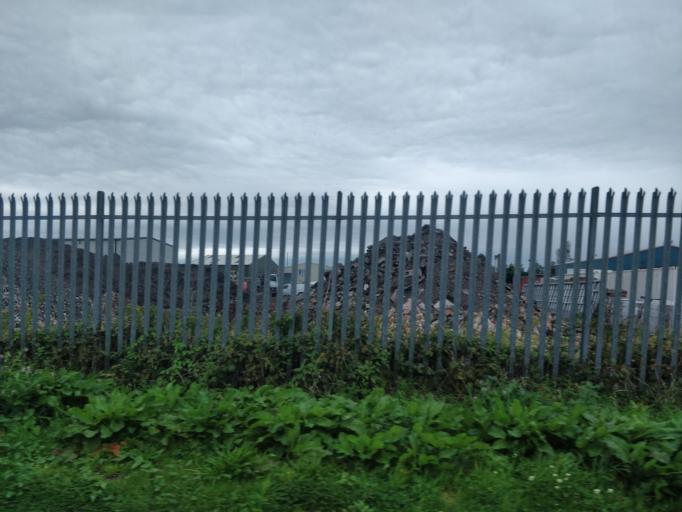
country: GB
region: England
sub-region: Lancashire
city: Ormskirk
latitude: 53.5967
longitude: -2.8617
